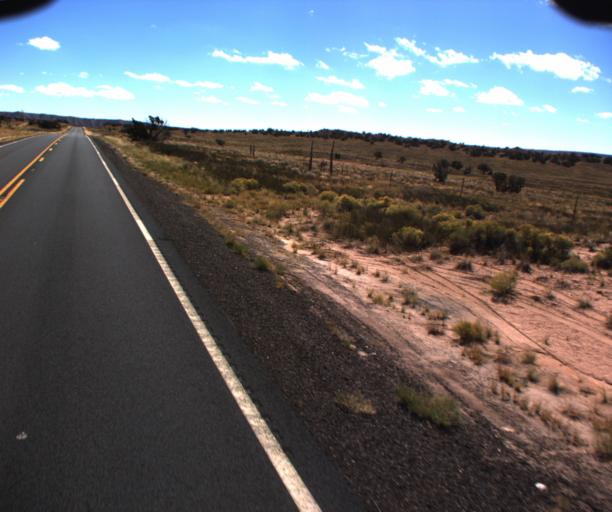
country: US
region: Arizona
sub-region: Apache County
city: Houck
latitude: 35.0744
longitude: -109.2937
